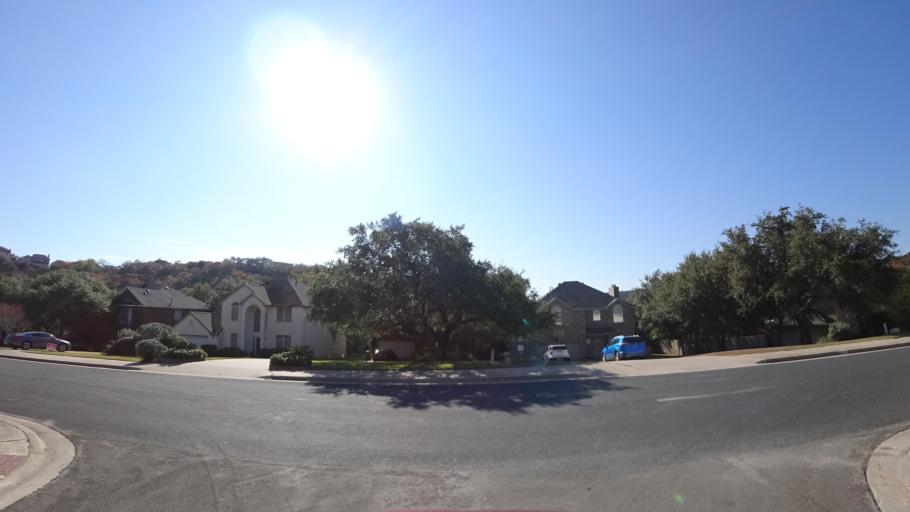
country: US
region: Texas
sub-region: Williamson County
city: Jollyville
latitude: 30.3956
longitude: -97.7725
